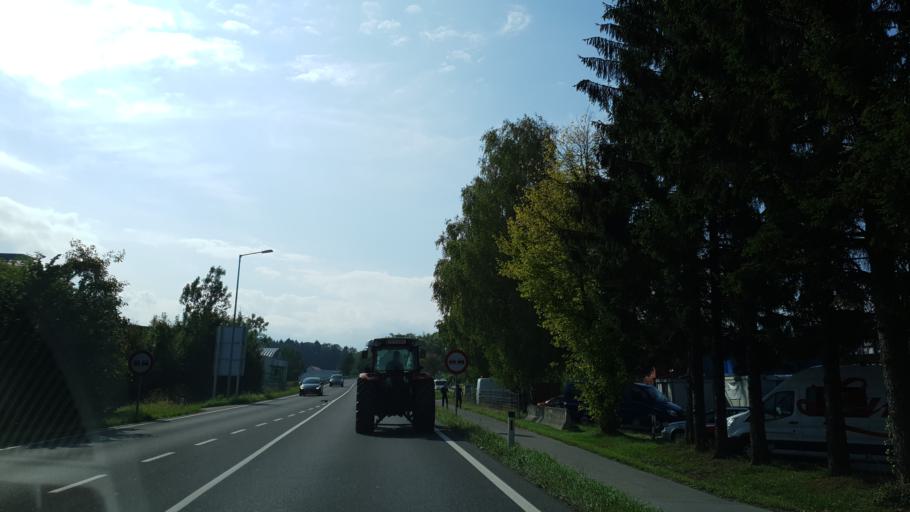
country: AT
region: Vorarlberg
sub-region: Politischer Bezirk Feldkirch
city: Klaus
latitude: 47.3004
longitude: 9.6210
